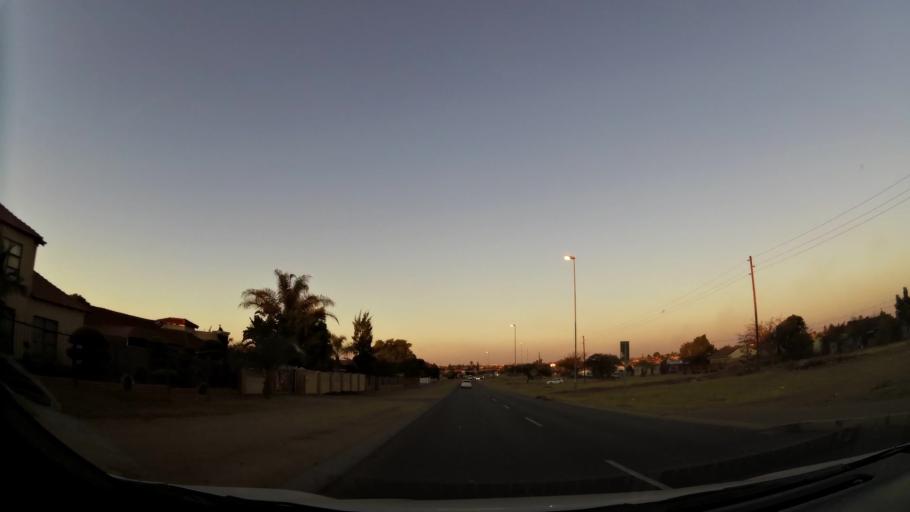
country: ZA
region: Limpopo
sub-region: Capricorn District Municipality
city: Polokwane
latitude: -23.8530
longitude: 29.3679
